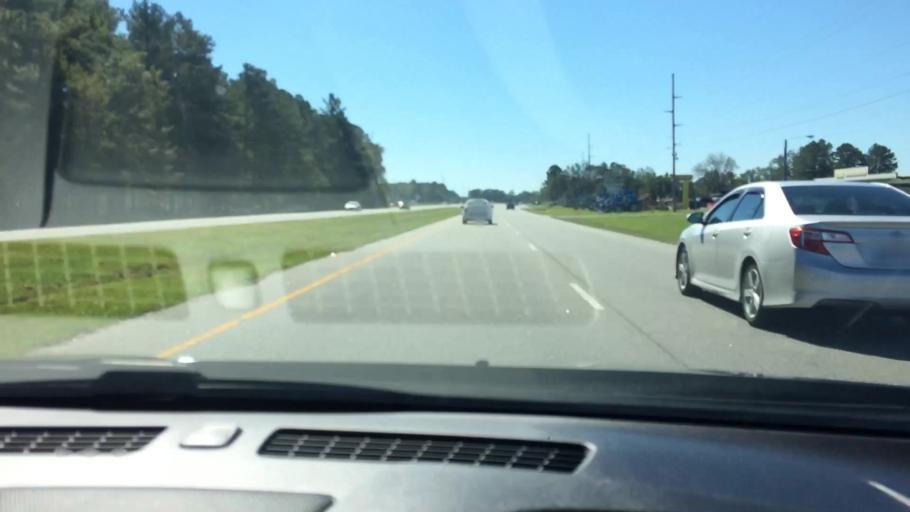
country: US
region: North Carolina
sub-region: Pitt County
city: Grifton
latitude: 35.4140
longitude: -77.4349
